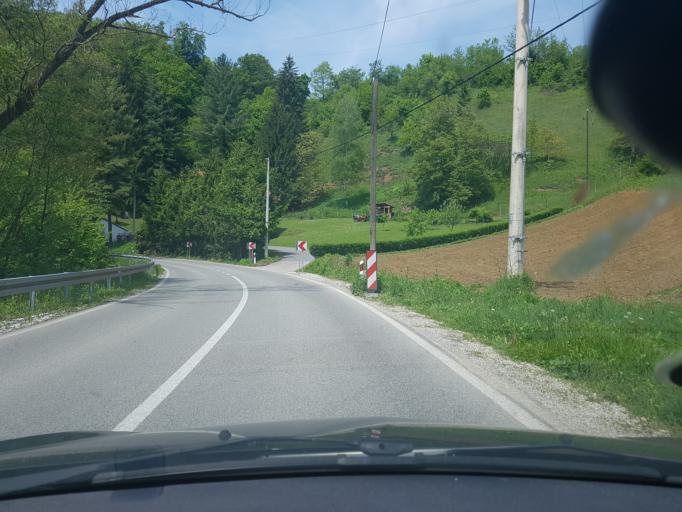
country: HR
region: Krapinsko-Zagorska
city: Pregrada
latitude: 46.1884
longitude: 15.7469
